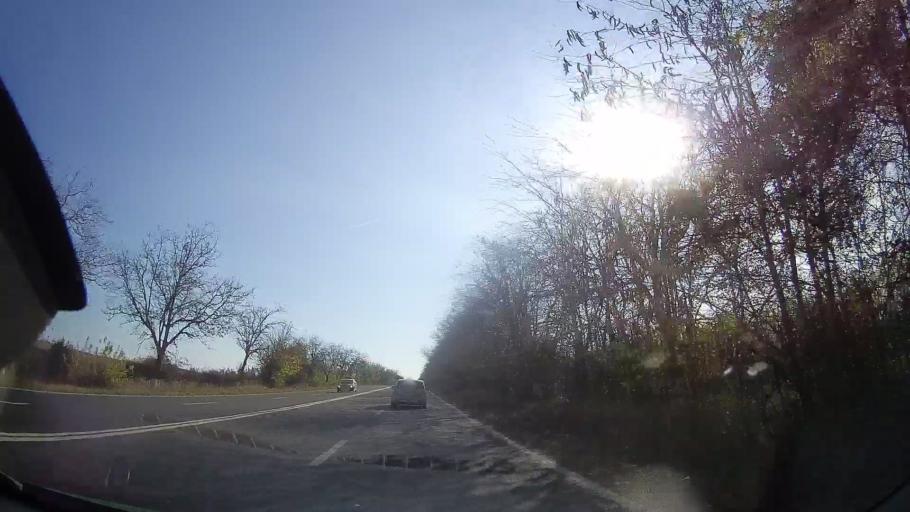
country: RO
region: Constanta
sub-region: Comuna Douazeci si Trei August
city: Douazeci si Trei August
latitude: 43.8945
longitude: 28.5718
